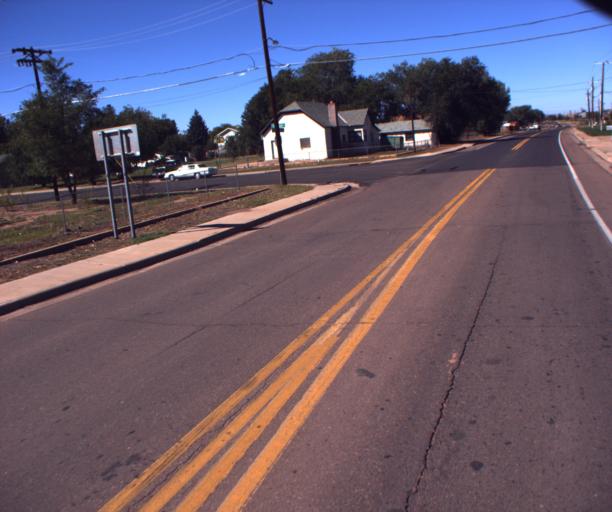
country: US
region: Arizona
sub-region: Navajo County
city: Snowflake
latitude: 34.5133
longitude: -110.0801
